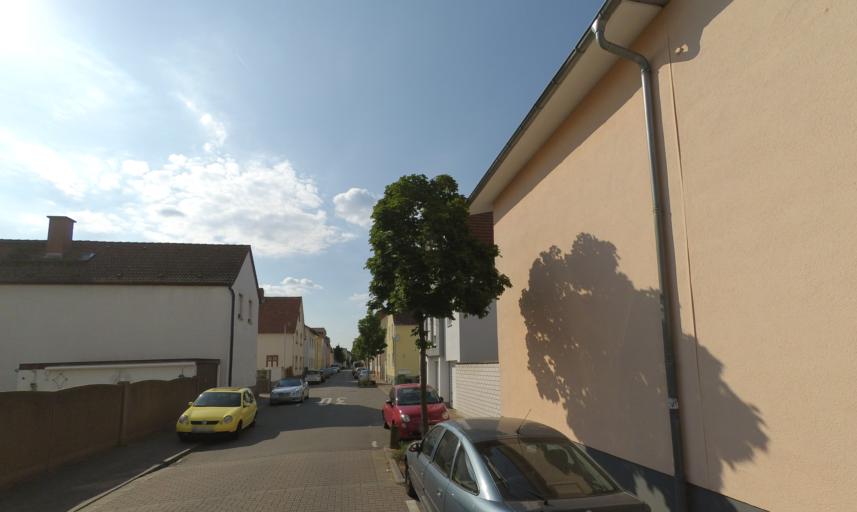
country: DE
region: Hesse
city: Viernheim
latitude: 49.5380
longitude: 8.5735
